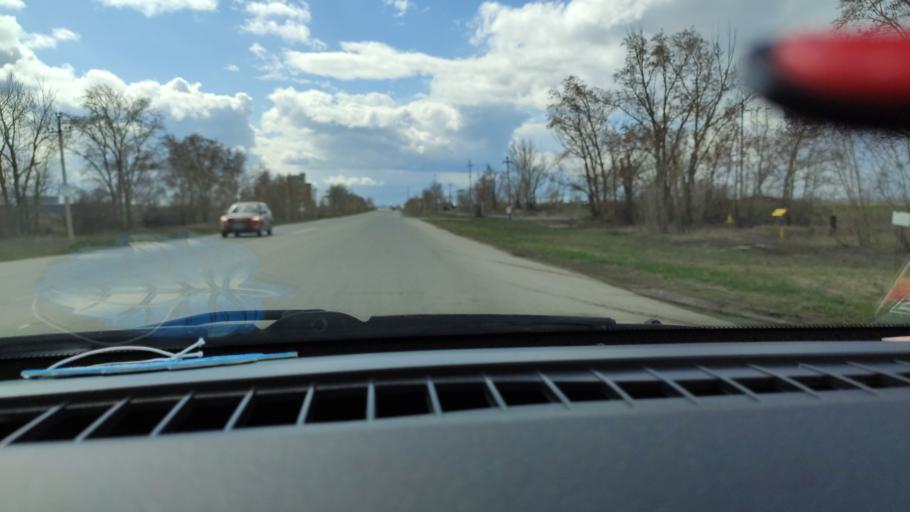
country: RU
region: Samara
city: Tol'yatti
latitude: 53.5850
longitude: 49.4047
